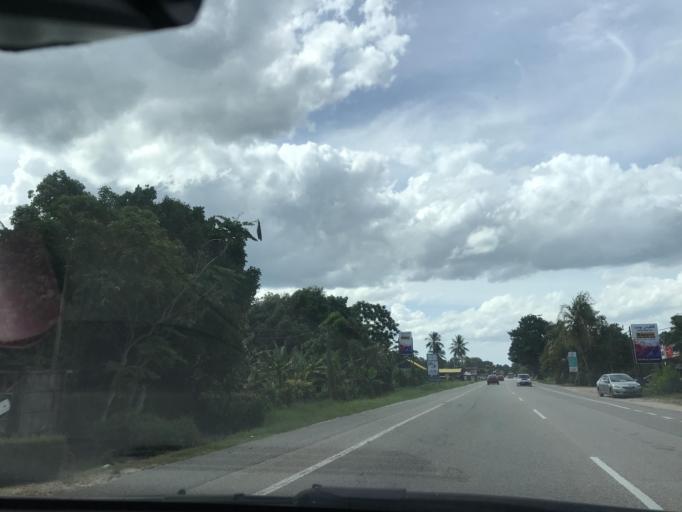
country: MY
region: Kelantan
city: Kampong Pangkal Kalong
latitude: 5.9083
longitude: 102.1874
